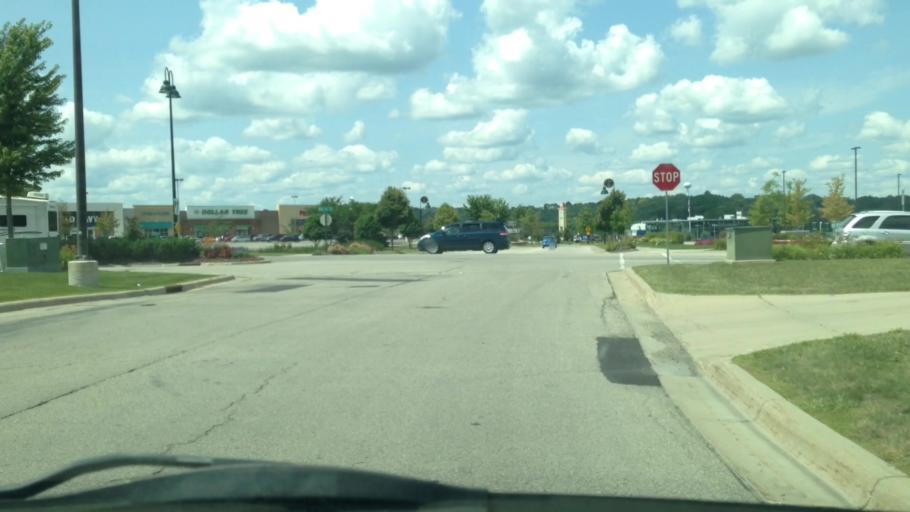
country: US
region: Minnesota
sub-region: Olmsted County
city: Rochester
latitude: 43.9551
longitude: -92.4618
